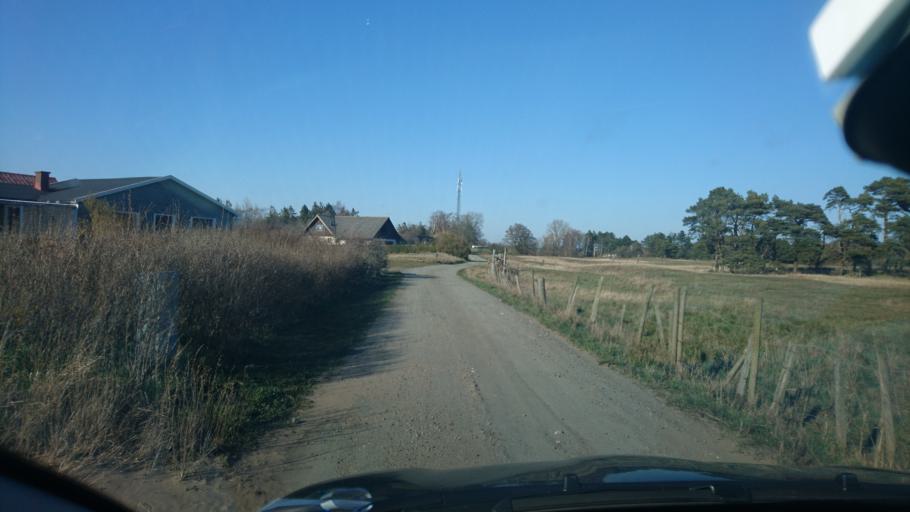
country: SE
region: Skane
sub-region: Simrishamns Kommun
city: Simrishamn
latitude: 55.4190
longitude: 14.2064
